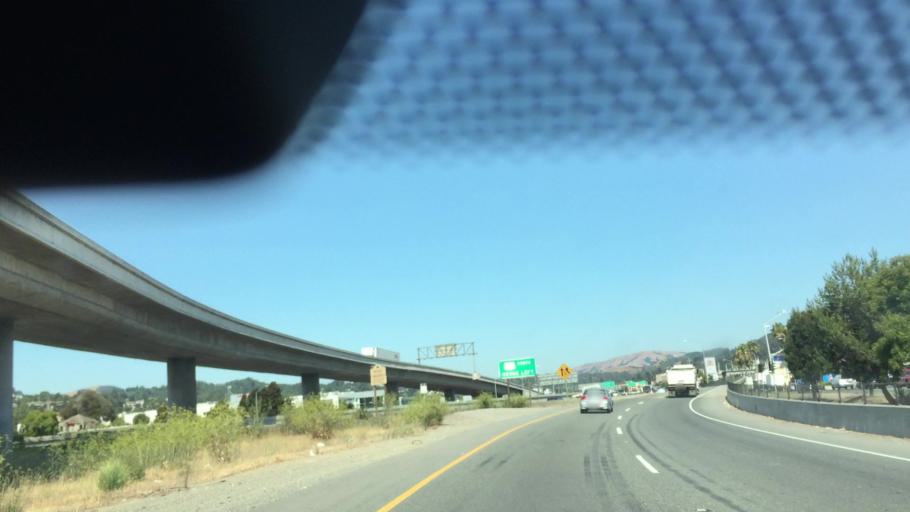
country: US
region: California
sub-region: Marin County
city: San Rafael
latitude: 37.9621
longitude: -122.5093
